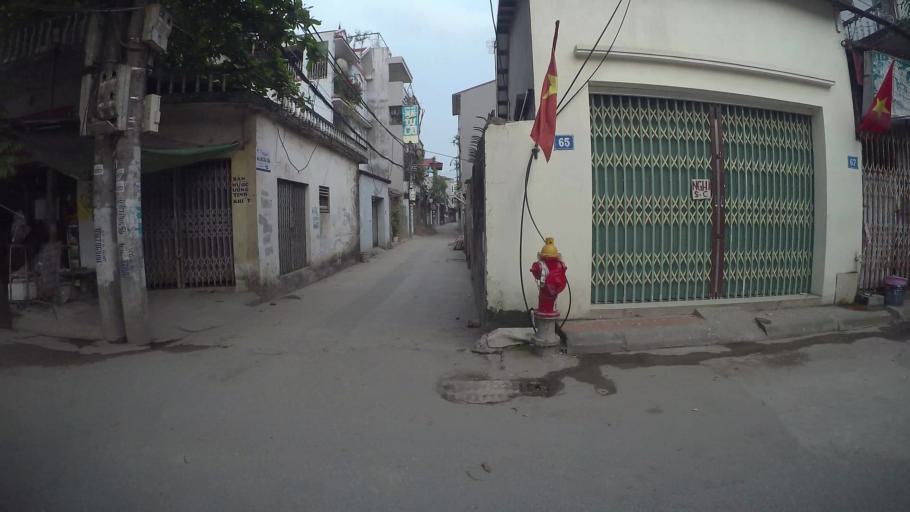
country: VN
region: Ha Noi
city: Trau Quy
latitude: 21.0745
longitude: 105.9018
